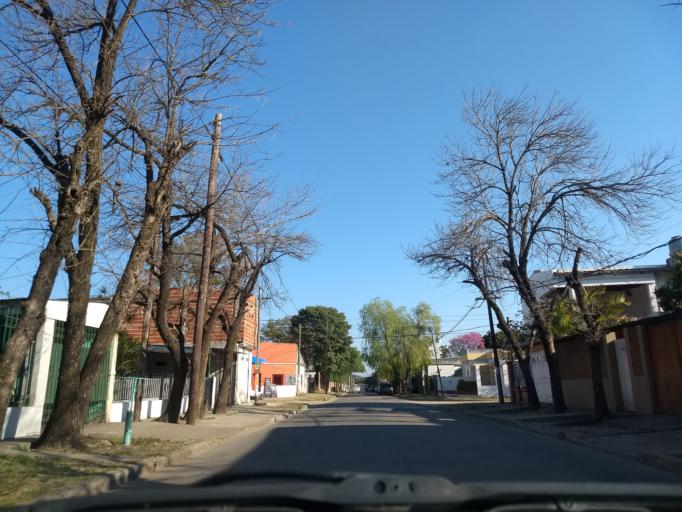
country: AR
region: Corrientes
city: Corrientes
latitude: -27.4746
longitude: -58.8066
